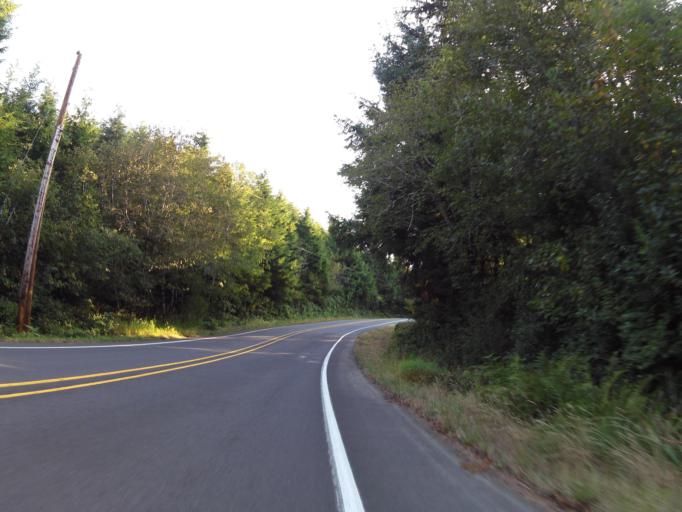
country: US
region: Oregon
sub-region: Lincoln County
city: Lincoln City
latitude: 44.9688
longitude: -123.9910
